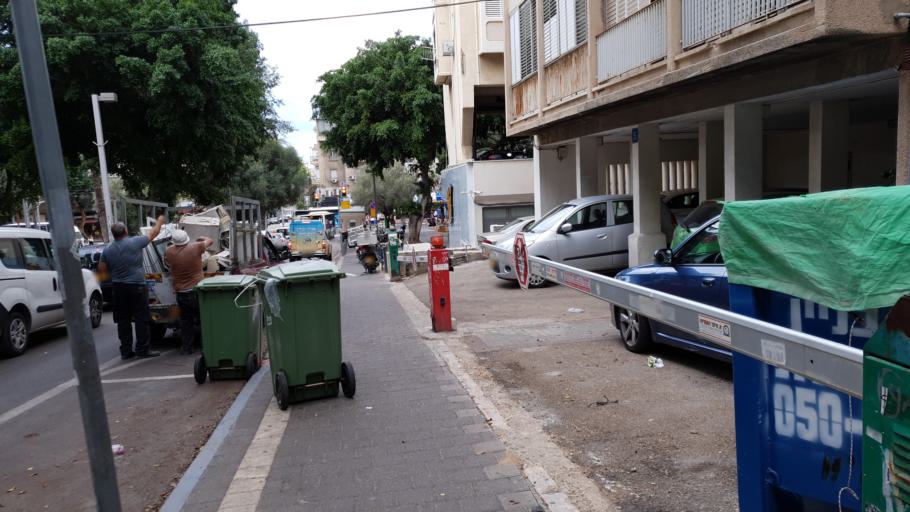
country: IL
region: Tel Aviv
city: Tel Aviv
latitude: 32.0736
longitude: 34.7764
